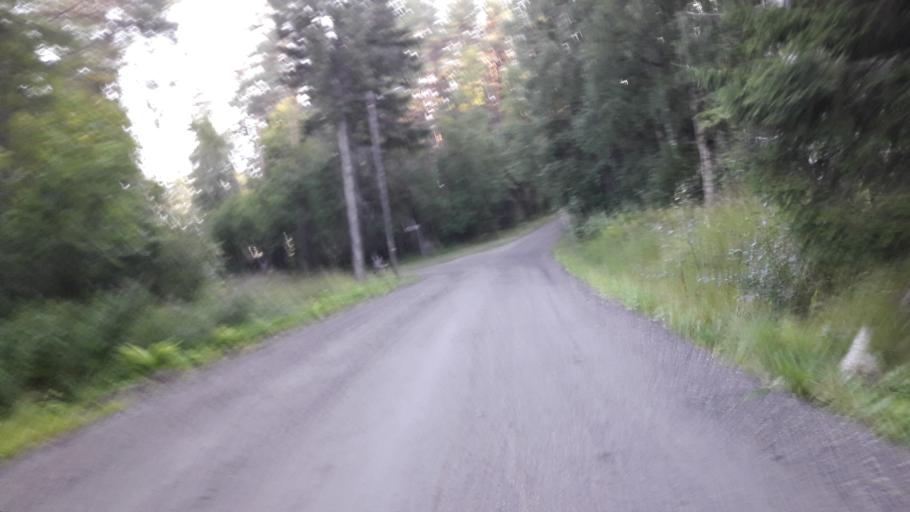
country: FI
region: North Karelia
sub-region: Joensuu
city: Joensuu
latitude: 62.6143
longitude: 29.6969
